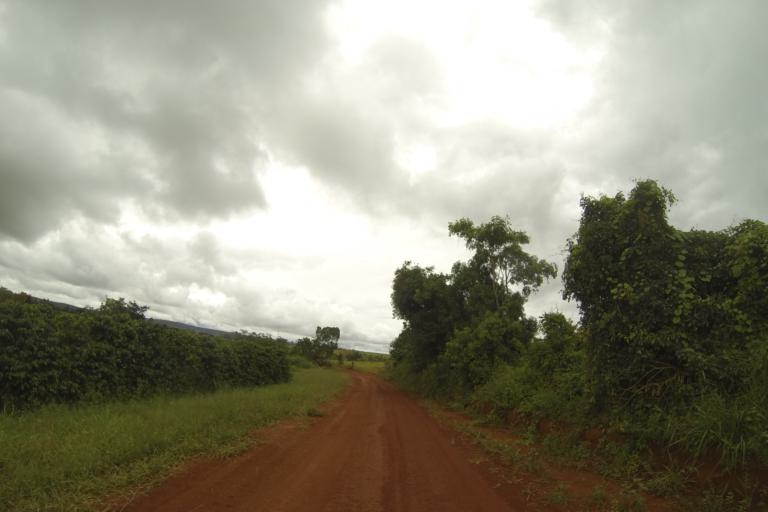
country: BR
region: Minas Gerais
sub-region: Ibia
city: Ibia
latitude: -19.7262
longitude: -46.5936
